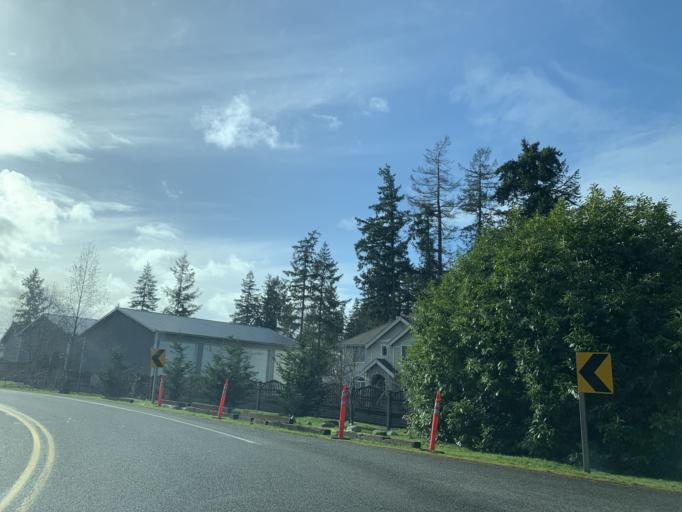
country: US
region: Washington
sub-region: King County
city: Lakeland South
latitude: 47.2884
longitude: -122.2976
